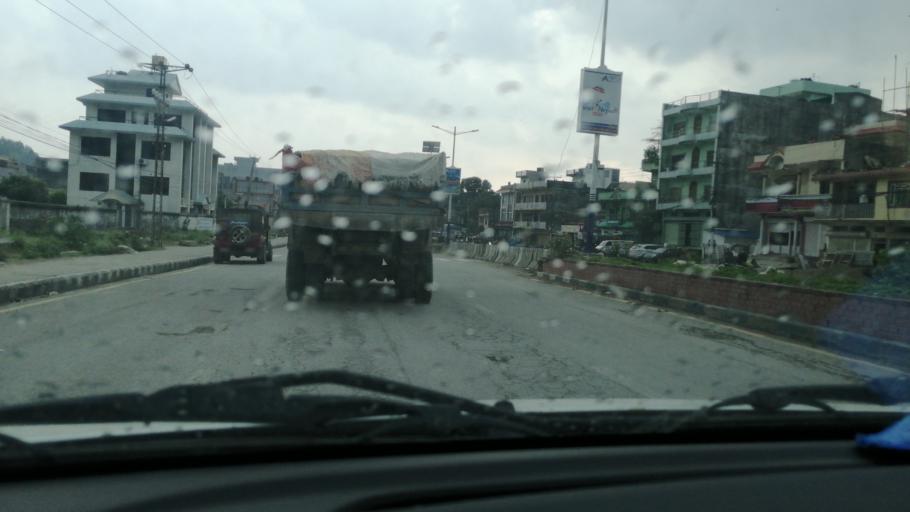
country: NP
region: Western Region
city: Butwal
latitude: 27.7082
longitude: 83.4678
